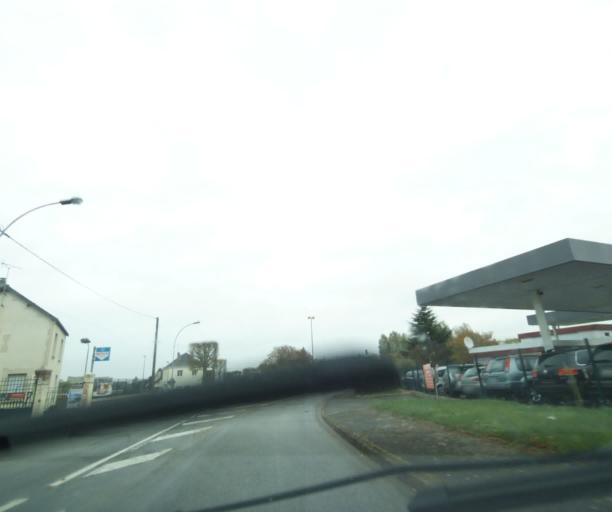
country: FR
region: Centre
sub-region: Departement d'Eure-et-Loir
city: Vernouillet
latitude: 48.7199
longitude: 1.3650
